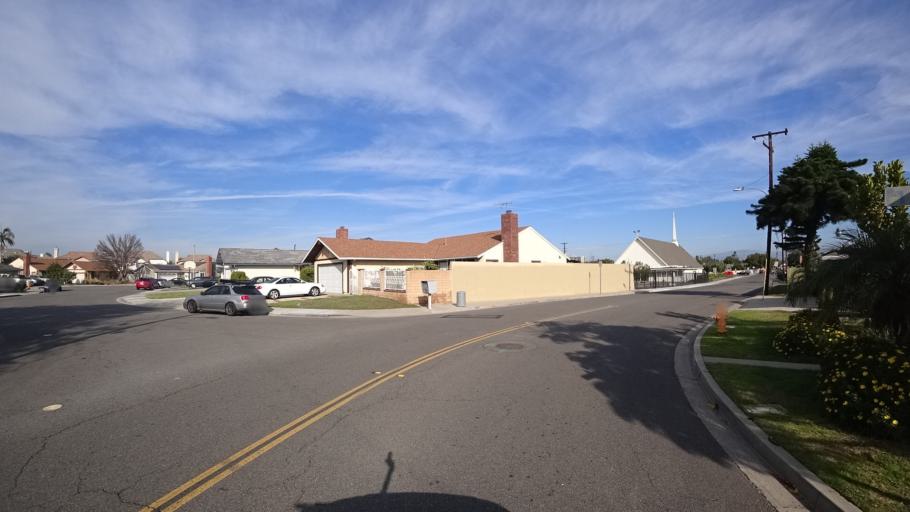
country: US
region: California
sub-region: Orange County
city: Garden Grove
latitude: 33.7707
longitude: -117.9046
